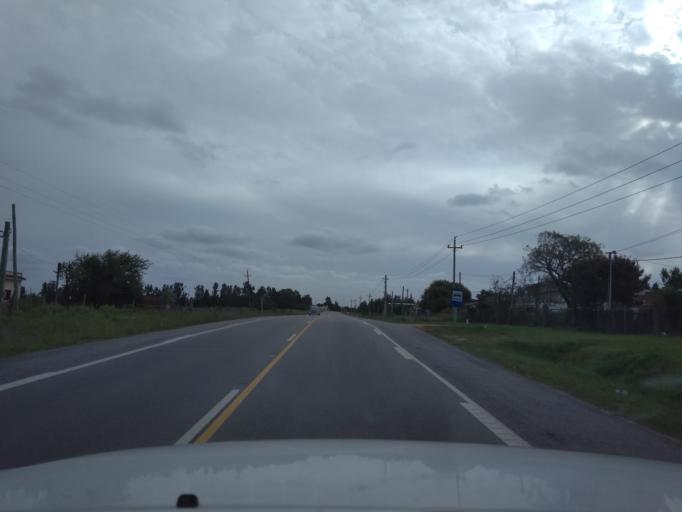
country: UY
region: Canelones
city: Joaquin Suarez
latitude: -34.7000
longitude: -56.0392
